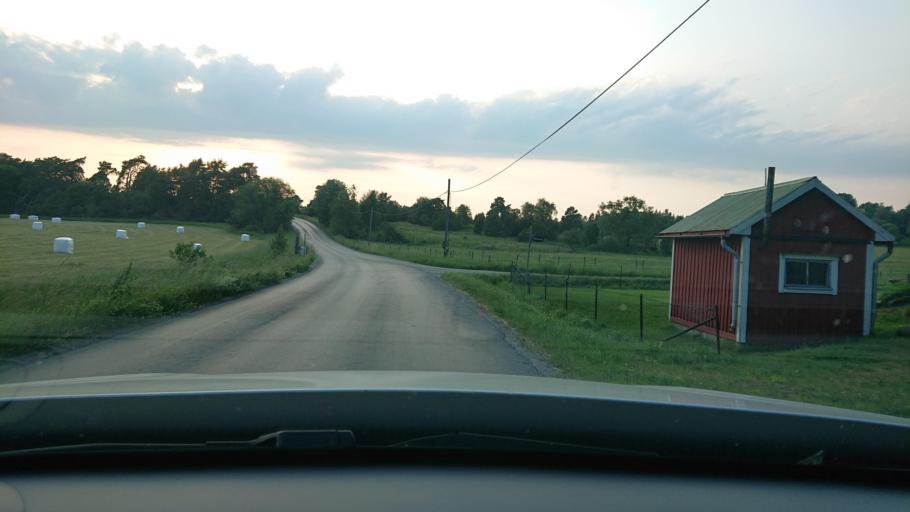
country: SE
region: Stockholm
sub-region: Osterakers Kommun
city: Akersberga
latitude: 59.5076
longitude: 18.3170
